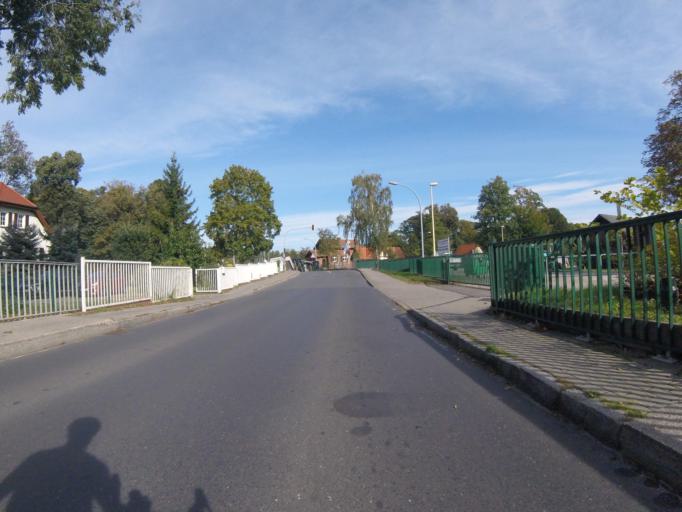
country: DE
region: Brandenburg
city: Konigs Wusterhausen
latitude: 52.2966
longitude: 13.6493
